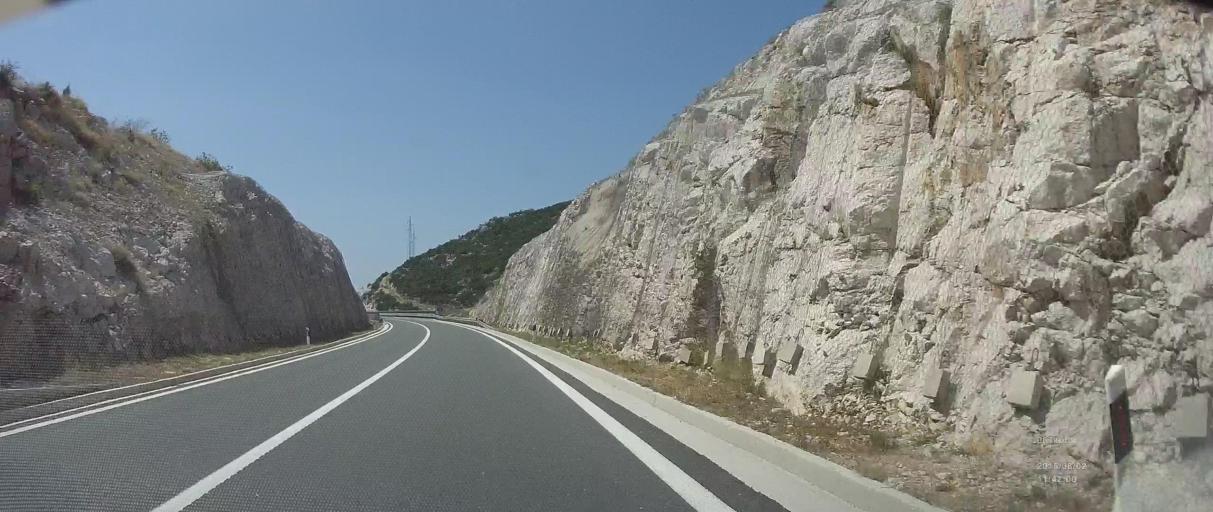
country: HR
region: Dubrovacko-Neretvanska
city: Komin
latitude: 43.0580
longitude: 17.4908
